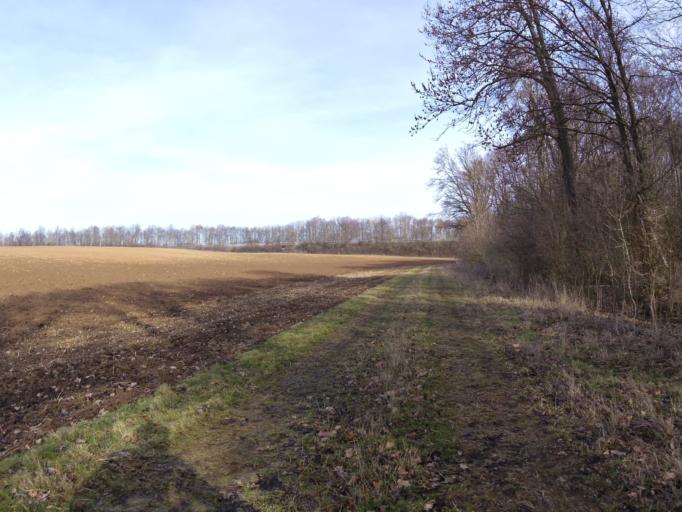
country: DE
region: Bavaria
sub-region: Regierungsbezirk Unterfranken
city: Kurnach
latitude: 49.8302
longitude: 10.0366
